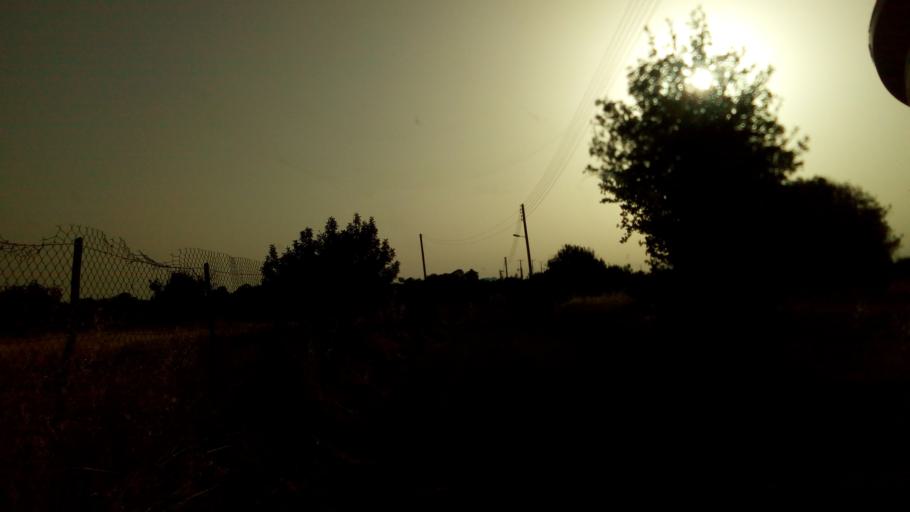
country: CY
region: Larnaka
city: Tersefanou
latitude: 34.8052
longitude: 33.5092
